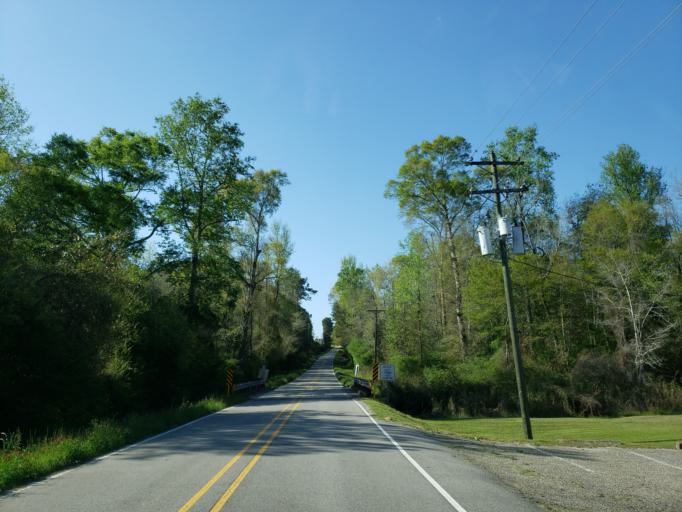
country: US
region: Mississippi
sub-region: Jones County
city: Ellisville
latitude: 31.6007
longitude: -89.3776
